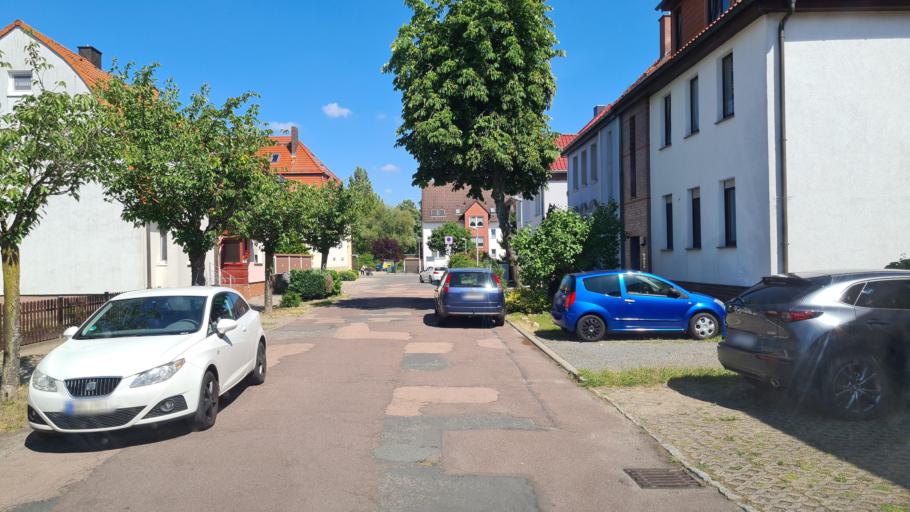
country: DE
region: Saxony-Anhalt
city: Wittenburg
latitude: 51.8731
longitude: 12.6564
